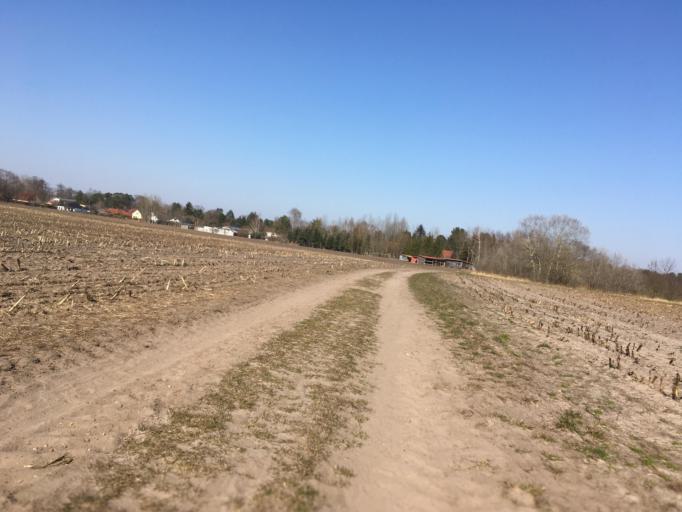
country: DE
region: Berlin
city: Buch
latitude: 52.6769
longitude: 13.4683
